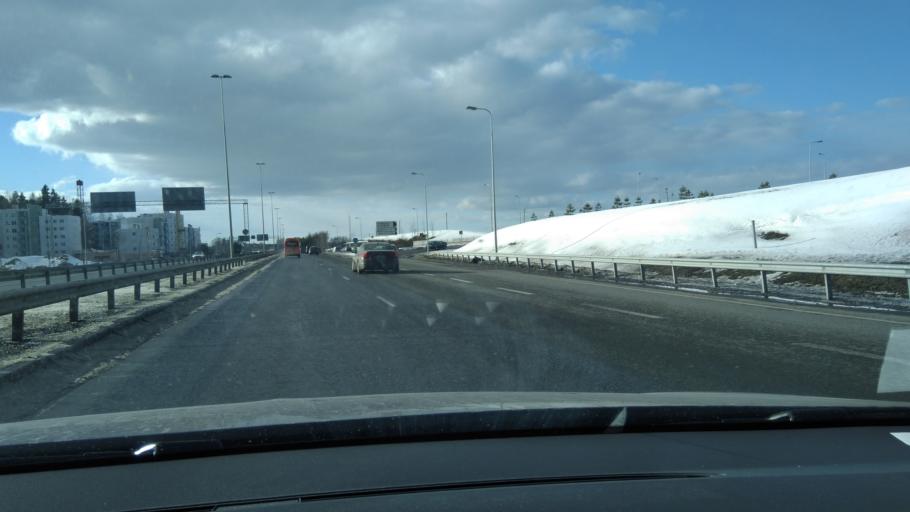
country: FI
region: Pirkanmaa
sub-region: Tampere
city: Tampere
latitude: 61.5033
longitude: 23.7248
